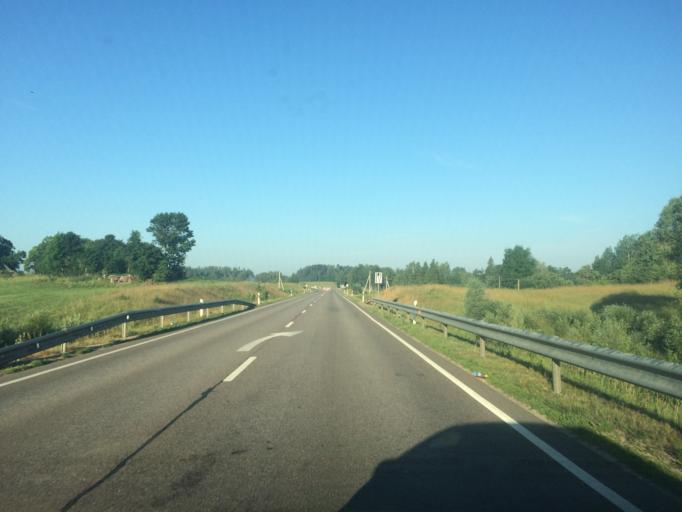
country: LT
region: Utenos apskritis
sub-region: Anyksciai
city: Anyksciai
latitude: 55.4138
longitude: 25.2057
